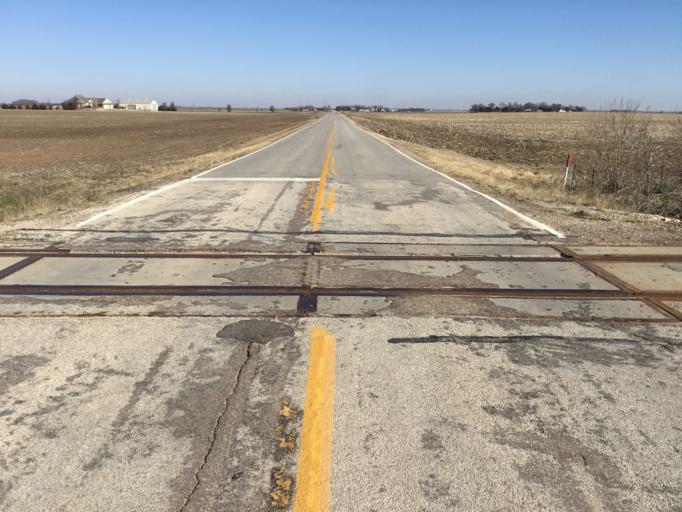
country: US
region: Kansas
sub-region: Sedgwick County
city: Colwich
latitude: 37.7860
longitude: -97.5896
